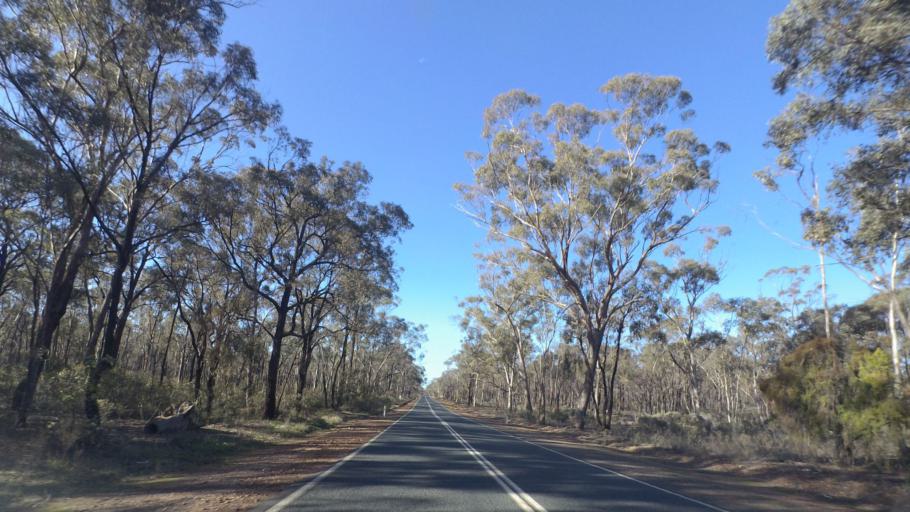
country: AU
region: Victoria
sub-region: Greater Bendigo
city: Epsom
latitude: -36.6686
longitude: 144.4254
